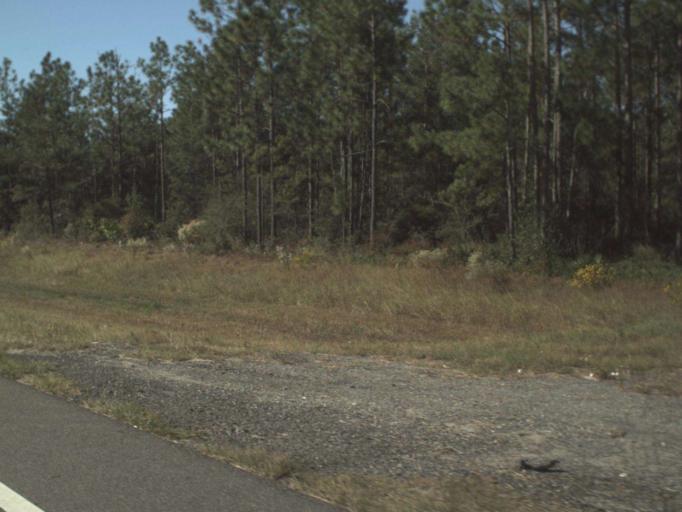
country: US
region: Florida
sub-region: Walton County
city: Freeport
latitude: 30.5031
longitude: -86.1165
